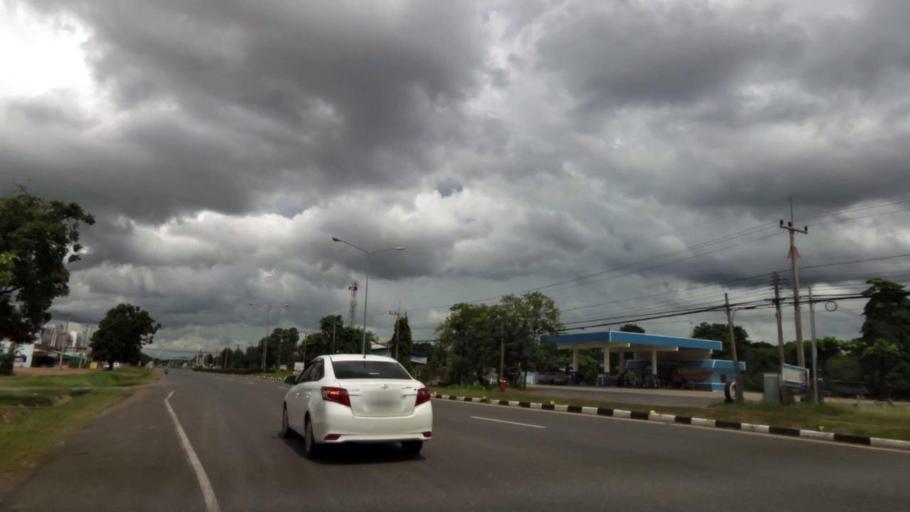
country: TH
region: Nakhon Sawan
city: Phai Sali
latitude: 15.5932
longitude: 100.6566
